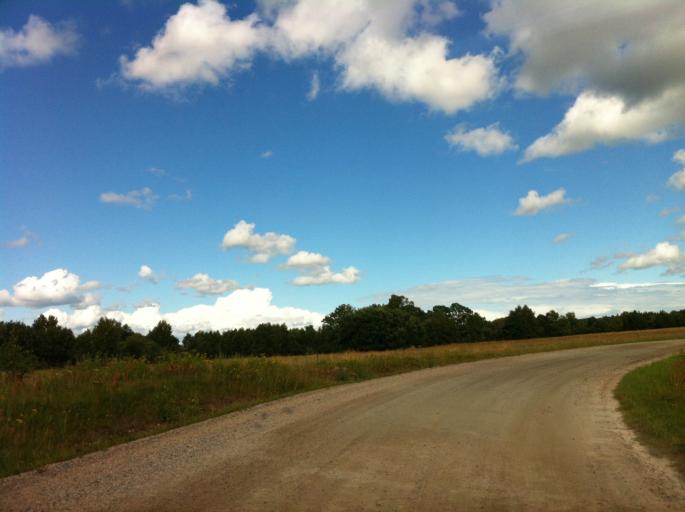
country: SE
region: Skane
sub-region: Hassleholms Kommun
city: Tormestorp
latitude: 56.1071
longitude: 13.7166
